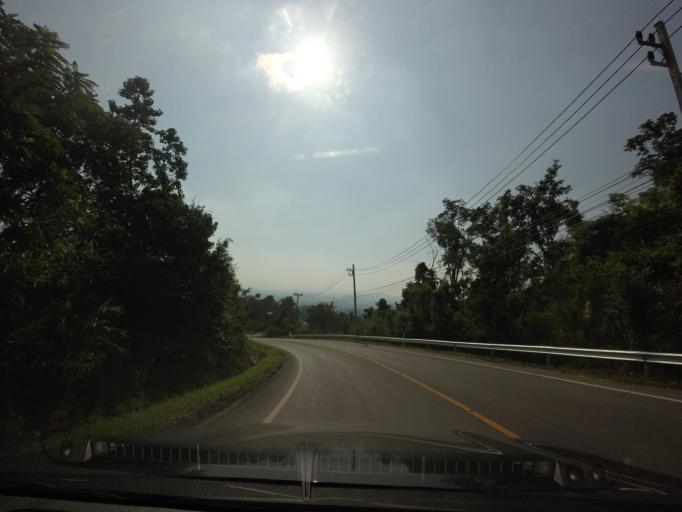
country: TH
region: Nan
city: Santi Suk
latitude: 18.9074
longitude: 100.8560
